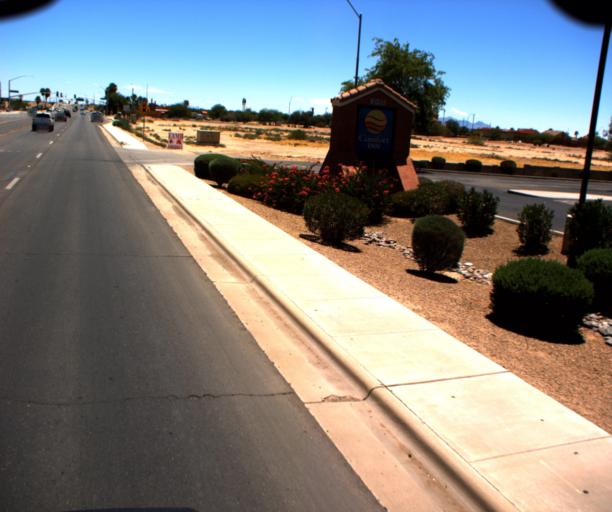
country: US
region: Arizona
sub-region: Pinal County
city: Casa Grande
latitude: 32.8796
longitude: -111.6948
